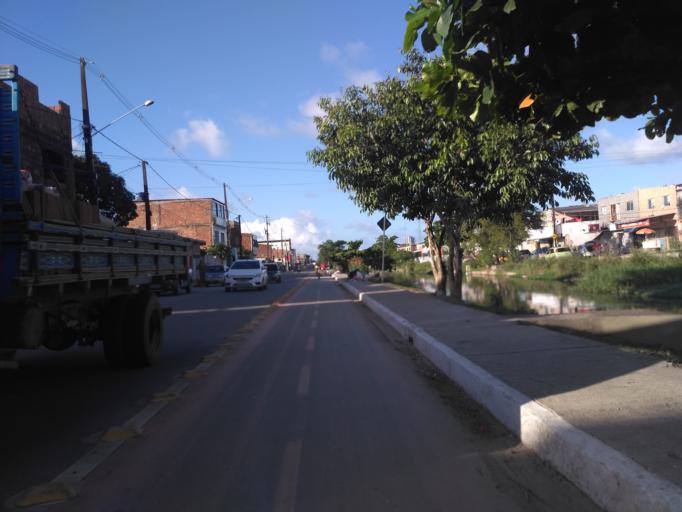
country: BR
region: Pernambuco
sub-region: Jaboatao Dos Guararapes
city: Jaboatao
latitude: -8.1832
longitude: -34.9369
